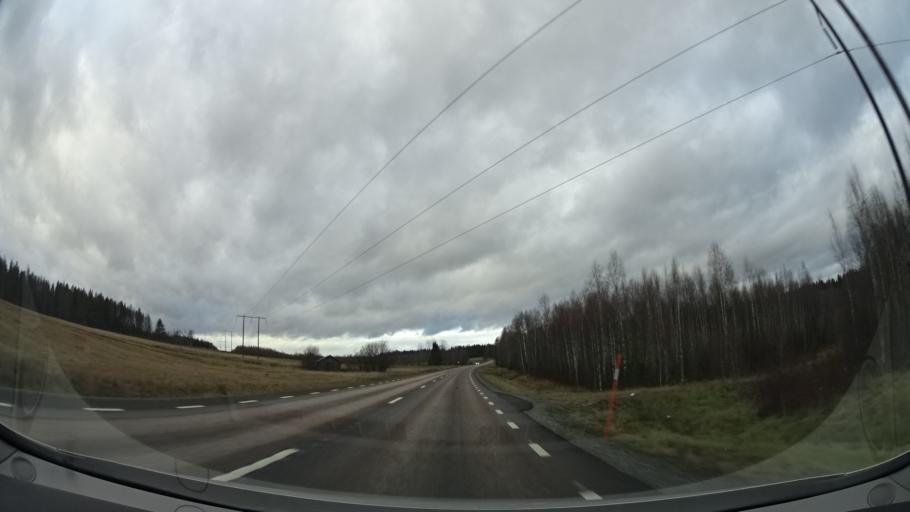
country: SE
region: Vaesterbotten
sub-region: Skelleftea Kommun
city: Viken
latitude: 64.7705
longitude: 20.8462
